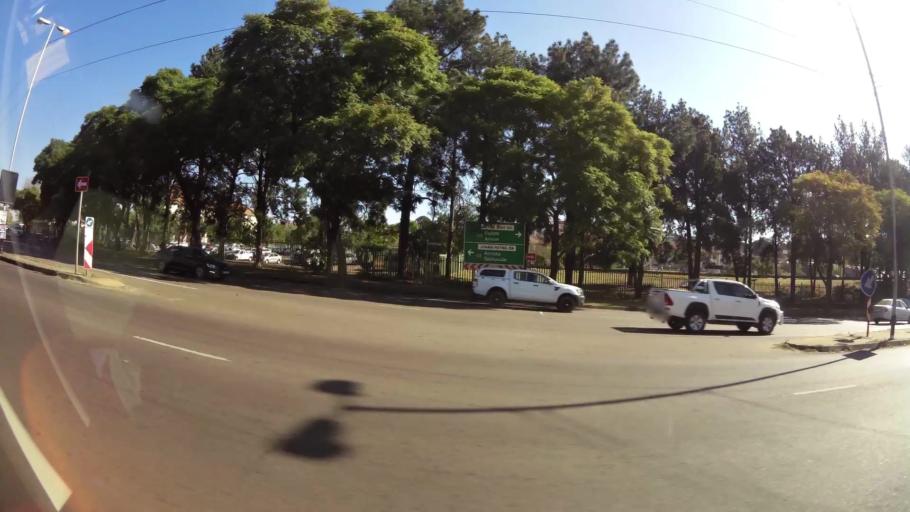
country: ZA
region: Gauteng
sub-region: City of Tshwane Metropolitan Municipality
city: Pretoria
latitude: -25.7318
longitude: 28.2048
